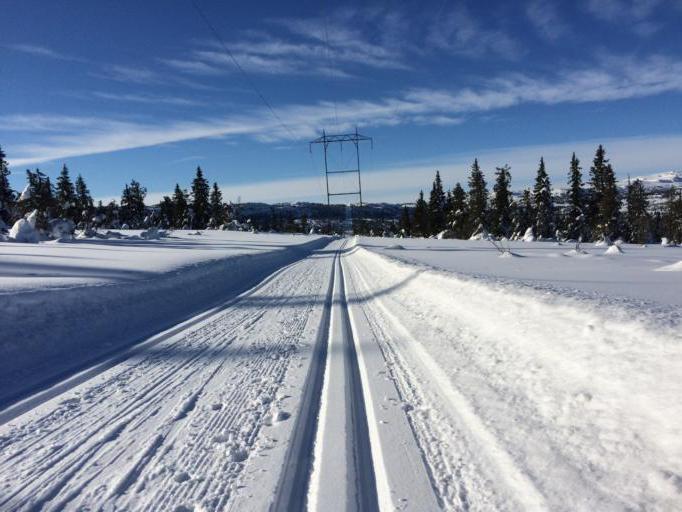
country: NO
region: Oppland
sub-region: Gausdal
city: Segalstad bru
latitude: 61.3155
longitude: 10.1012
